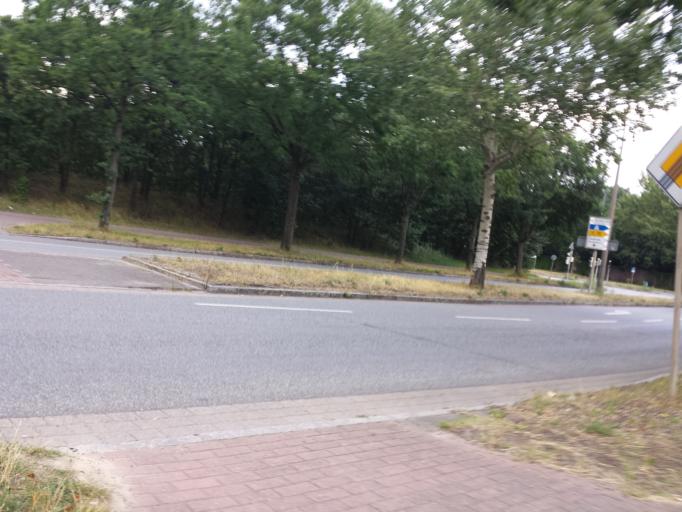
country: DE
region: Lower Saxony
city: Stuhr
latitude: 53.0810
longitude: 8.7542
